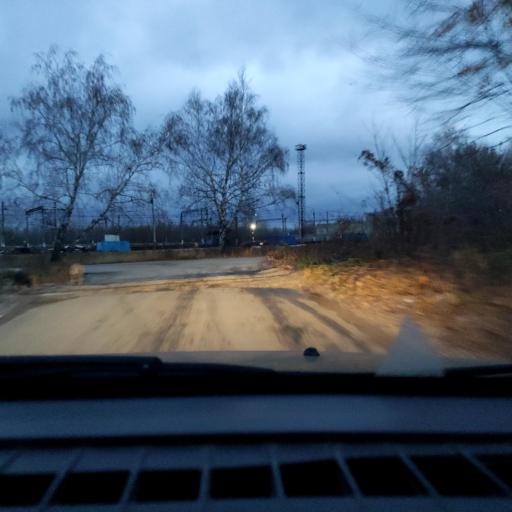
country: RU
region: Samara
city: Tol'yatti
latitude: 53.5635
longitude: 49.3152
